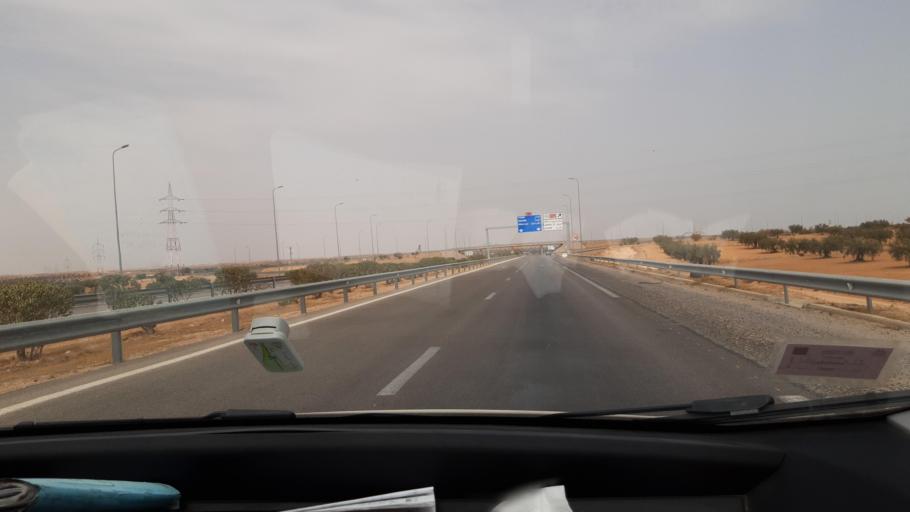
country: TN
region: Safaqis
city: Sfax
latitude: 34.7243
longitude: 10.5856
